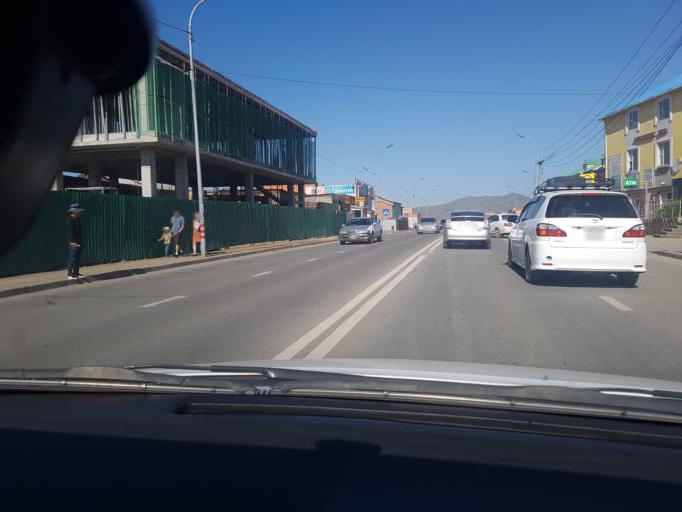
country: MN
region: Ulaanbaatar
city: Ulaanbaatar
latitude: 47.9537
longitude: 106.8525
